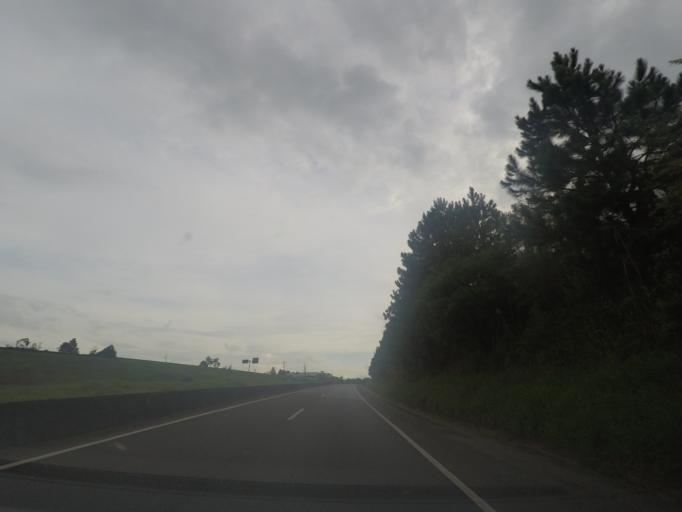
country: BR
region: Parana
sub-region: Quatro Barras
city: Quatro Barras
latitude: -25.3455
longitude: -49.0449
